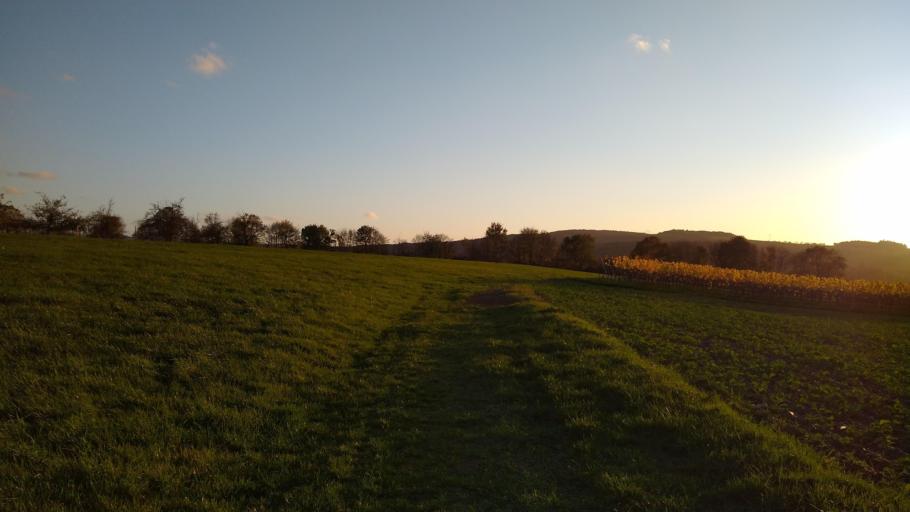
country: DE
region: Rheinland-Pfalz
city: Bekond
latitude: 49.8544
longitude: 6.8204
